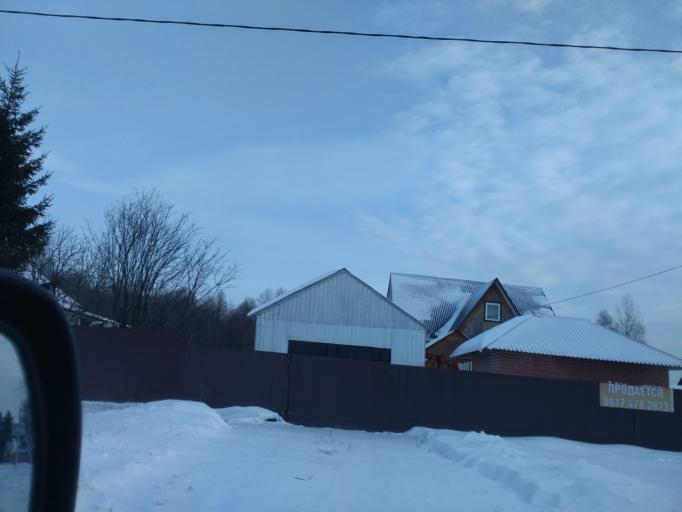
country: RU
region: Bashkortostan
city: Iglino
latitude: 54.7432
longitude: 56.5968
